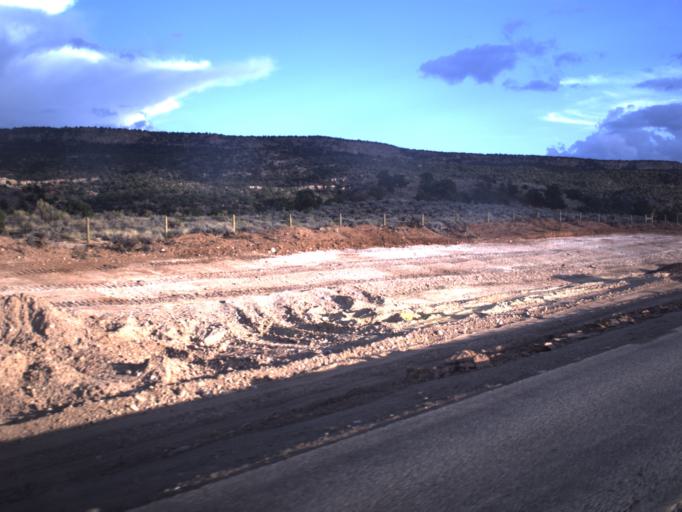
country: US
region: Utah
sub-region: San Juan County
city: Monticello
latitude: 38.0359
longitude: -109.3448
